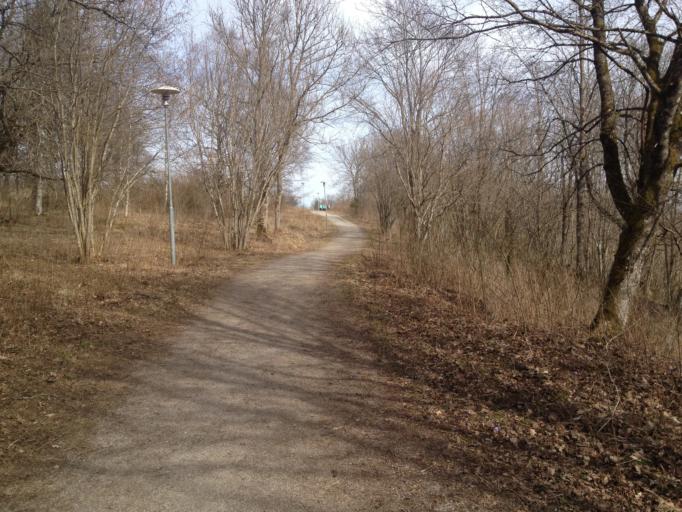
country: SE
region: Vaestra Goetaland
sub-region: Falkopings Kommun
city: Falkoeping
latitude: 58.1800
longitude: 13.5364
